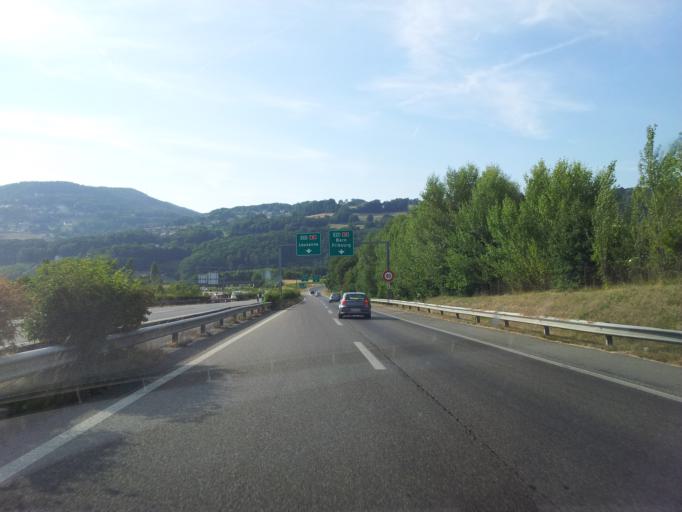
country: CH
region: Vaud
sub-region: Riviera-Pays-d'Enhaut District
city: La Tour-de-Peilz
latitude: 46.4720
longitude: 6.8660
